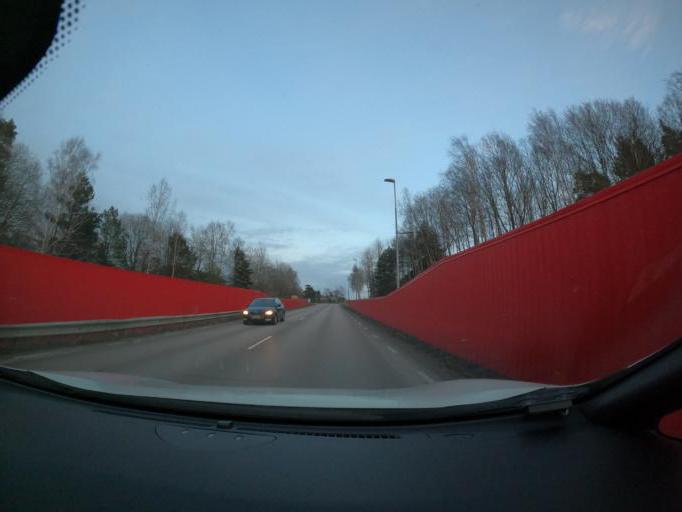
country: SE
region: Vaestra Goetaland
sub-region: Harryda Kommun
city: Molnlycke
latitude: 57.6540
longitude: 12.1321
